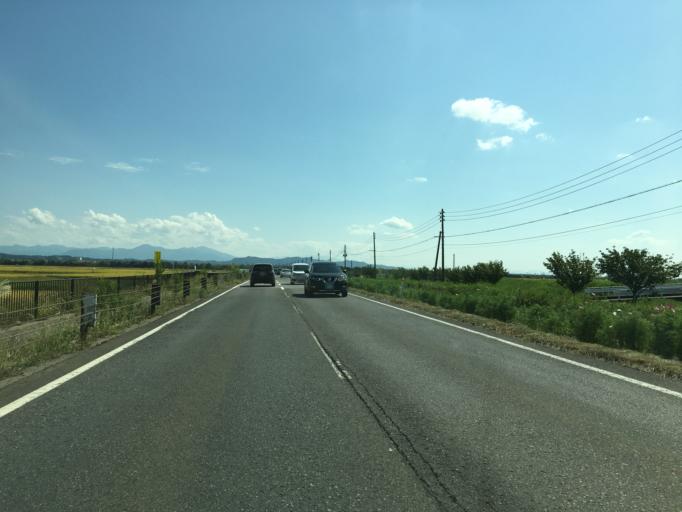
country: JP
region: Niigata
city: Niitsu-honcho
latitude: 37.8298
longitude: 139.0974
